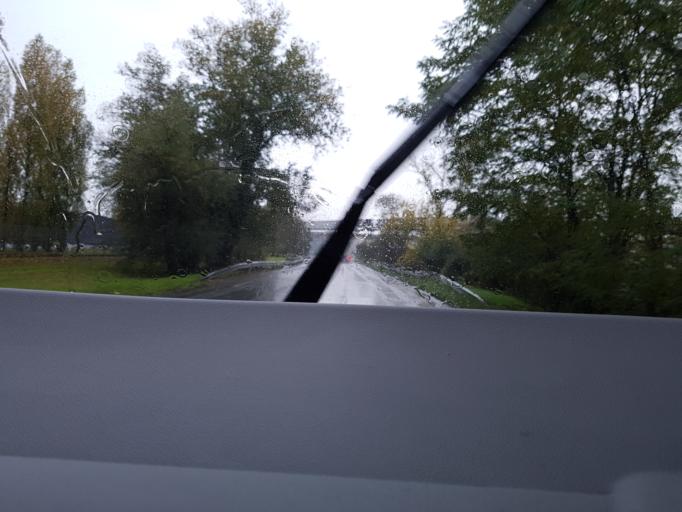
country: FR
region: Aquitaine
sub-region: Departement de la Gironde
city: Bassens
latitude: 44.9120
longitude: -0.5377
